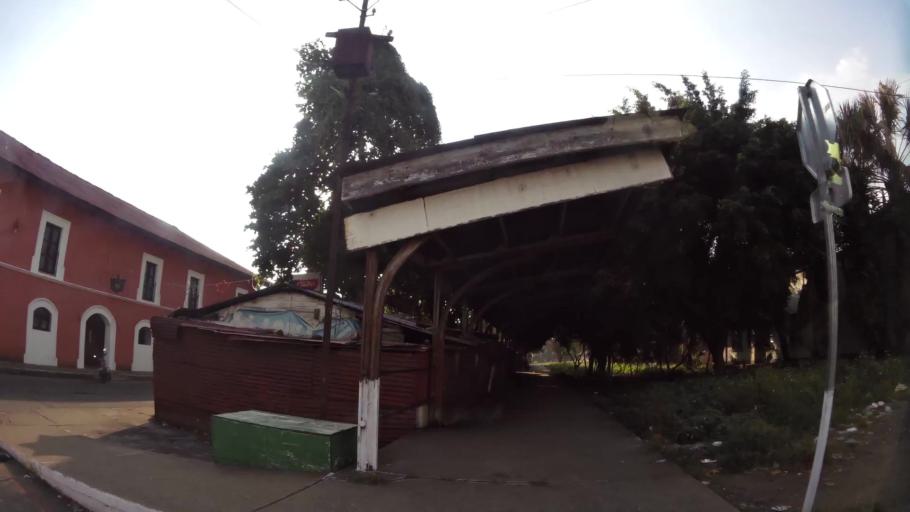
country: GT
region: Retalhuleu
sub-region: Municipio de Retalhuleu
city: Retalhuleu
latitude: 14.5381
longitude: -91.6797
